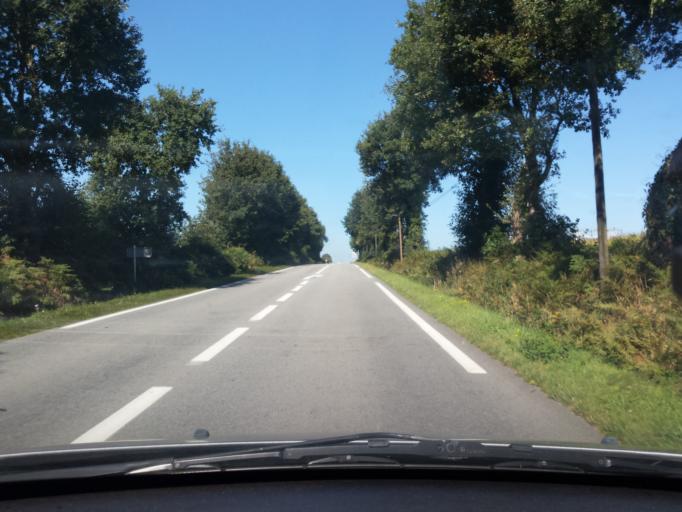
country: FR
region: Brittany
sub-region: Departement du Morbihan
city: Saint-Thuriau
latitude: 48.0245
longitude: -2.9133
